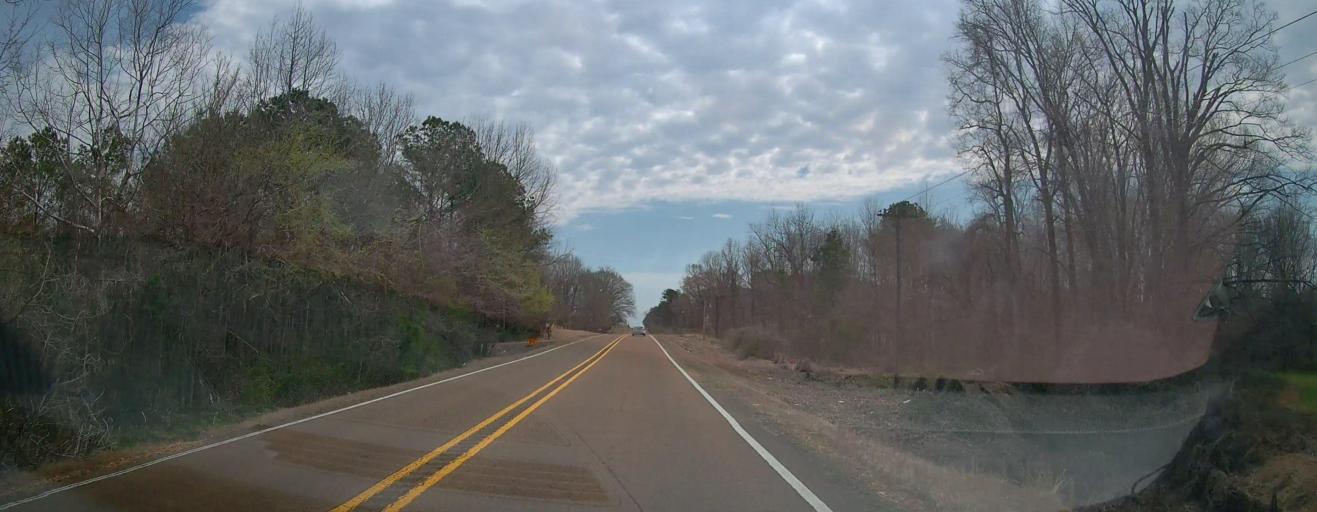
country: US
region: Mississippi
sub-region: Marshall County
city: Holly Springs
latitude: 34.8202
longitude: -89.5412
